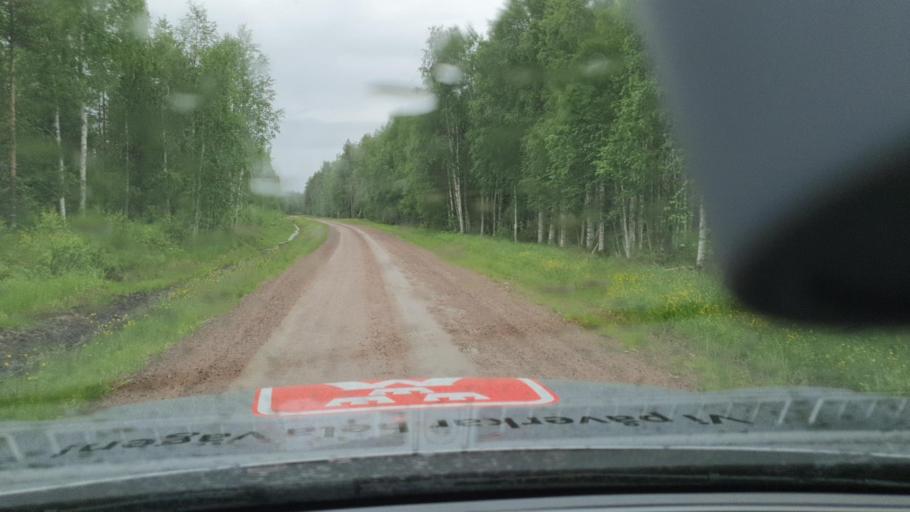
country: SE
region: Norrbotten
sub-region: Overkalix Kommun
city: OEverkalix
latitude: 66.5514
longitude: 22.7459
